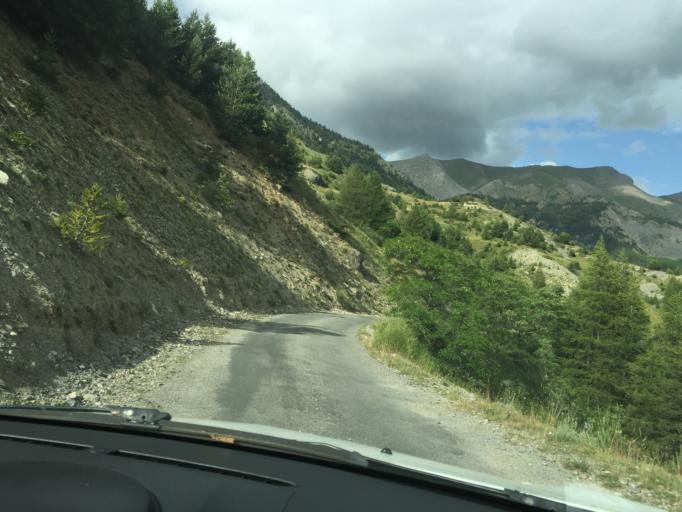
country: FR
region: Provence-Alpes-Cote d'Azur
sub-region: Departement des Hautes-Alpes
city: Guillestre
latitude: 44.6730
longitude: 6.7868
